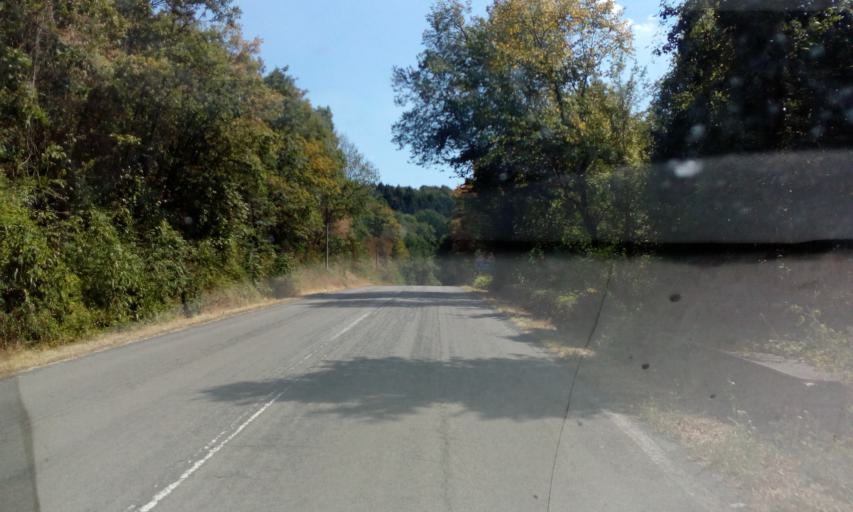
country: BE
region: Wallonia
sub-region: Province de Namur
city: Houyet
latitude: 50.1937
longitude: 5.0480
